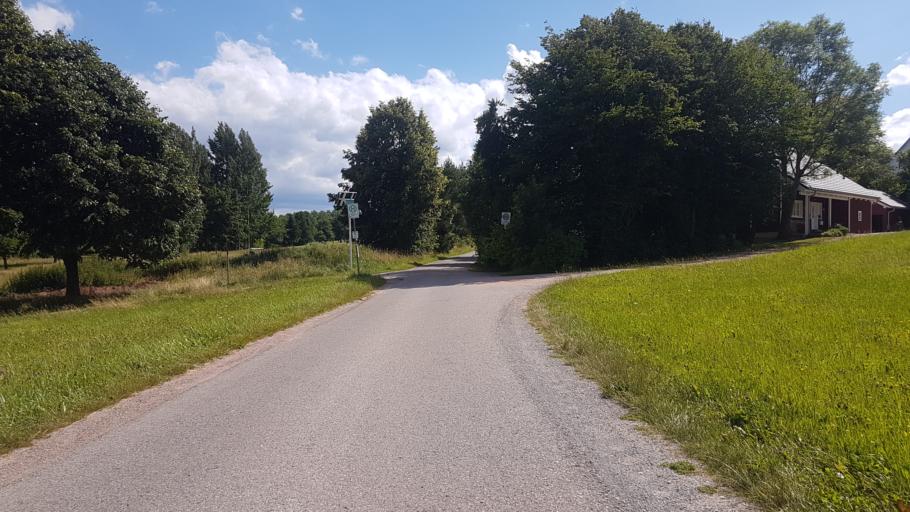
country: DE
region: Baden-Wuerttemberg
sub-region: Freiburg Region
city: Konigsfeld im Schwarzwald
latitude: 48.1488
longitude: 8.4082
